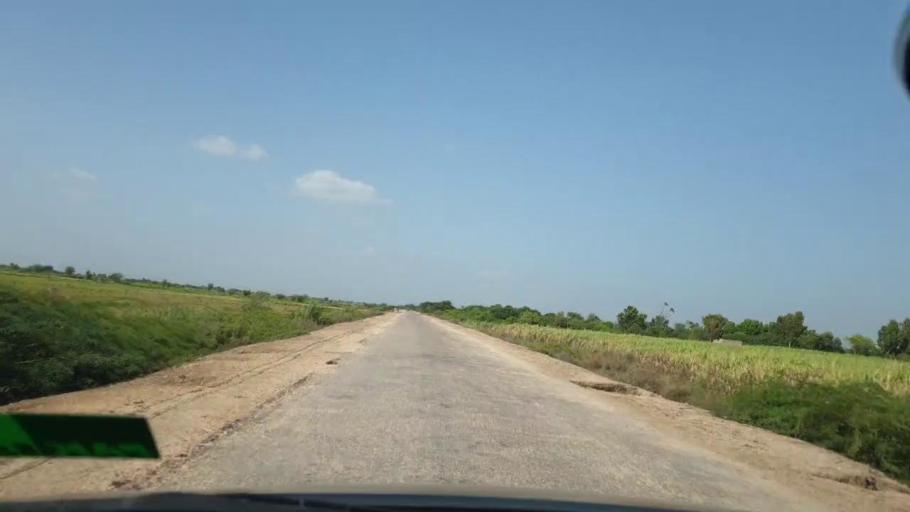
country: PK
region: Sindh
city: Tando Bago
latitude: 24.6887
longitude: 69.1883
